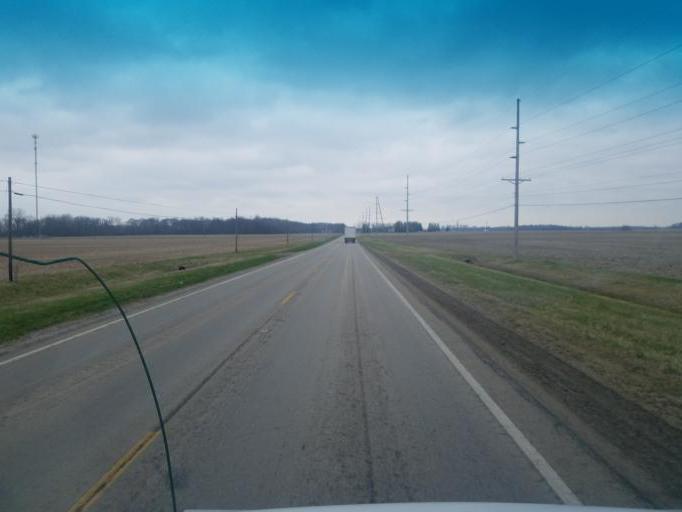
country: US
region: Ohio
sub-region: Defiance County
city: Hicksville
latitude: 41.2638
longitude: -84.7609
